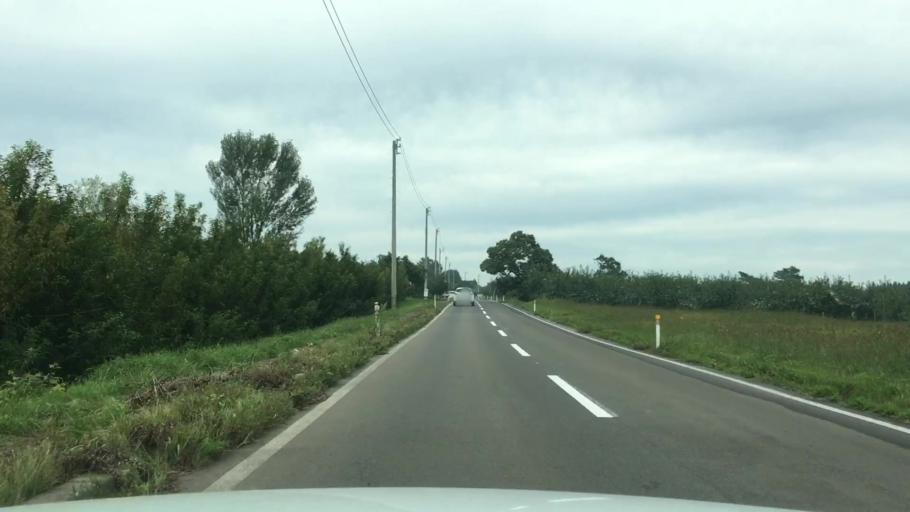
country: JP
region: Aomori
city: Hirosaki
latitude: 40.6694
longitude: 140.3890
